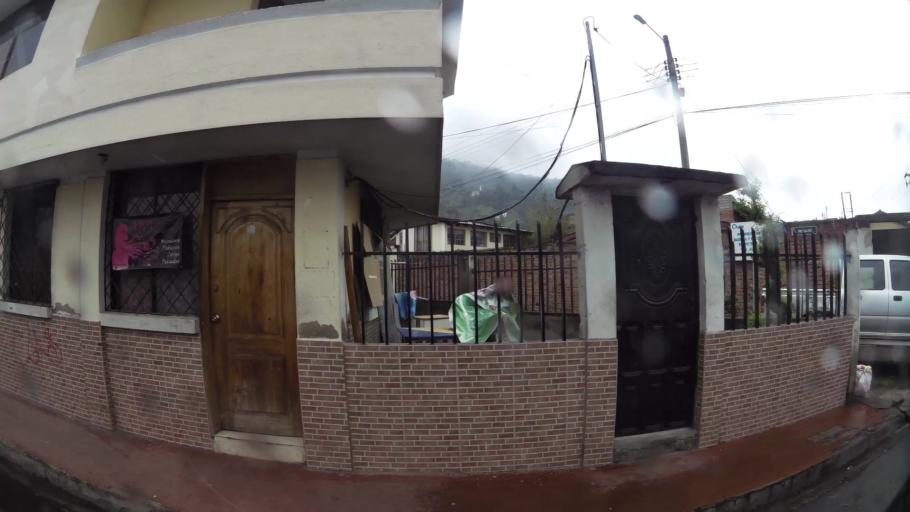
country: EC
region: Pichincha
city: Sangolqui
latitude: -0.2851
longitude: -78.4419
